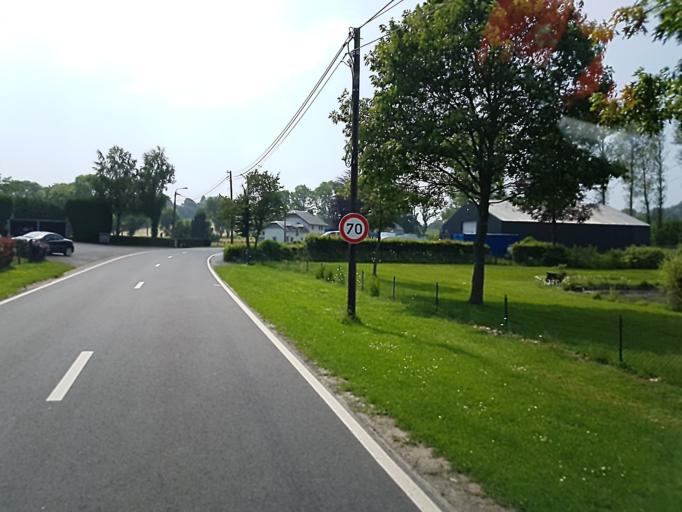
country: BE
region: Wallonia
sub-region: Province de Liege
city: Lierneux
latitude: 50.3221
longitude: 5.7414
